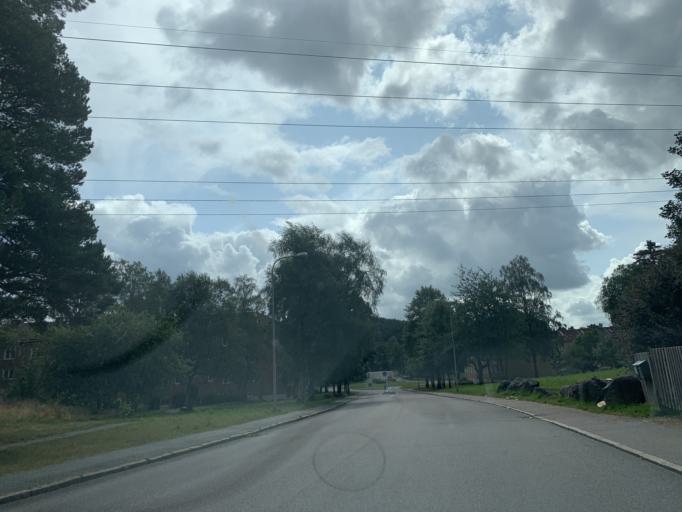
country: SE
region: Vaestra Goetaland
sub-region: Goteborg
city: Eriksbo
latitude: 57.7590
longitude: 12.0418
